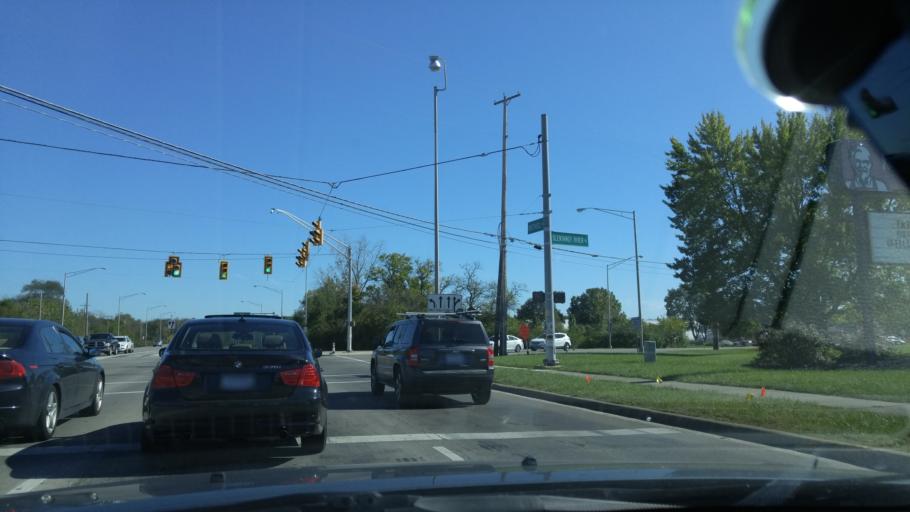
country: US
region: Ohio
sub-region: Franklin County
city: Worthington
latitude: 40.0630
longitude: -83.0380
